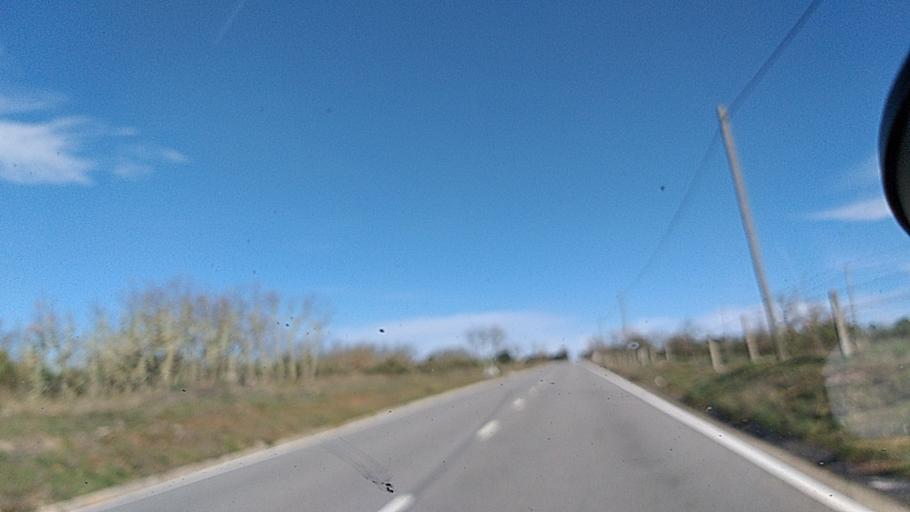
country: ES
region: Castille and Leon
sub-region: Provincia de Salamanca
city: Fuentes de Onoro
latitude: 40.6156
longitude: -6.8665
